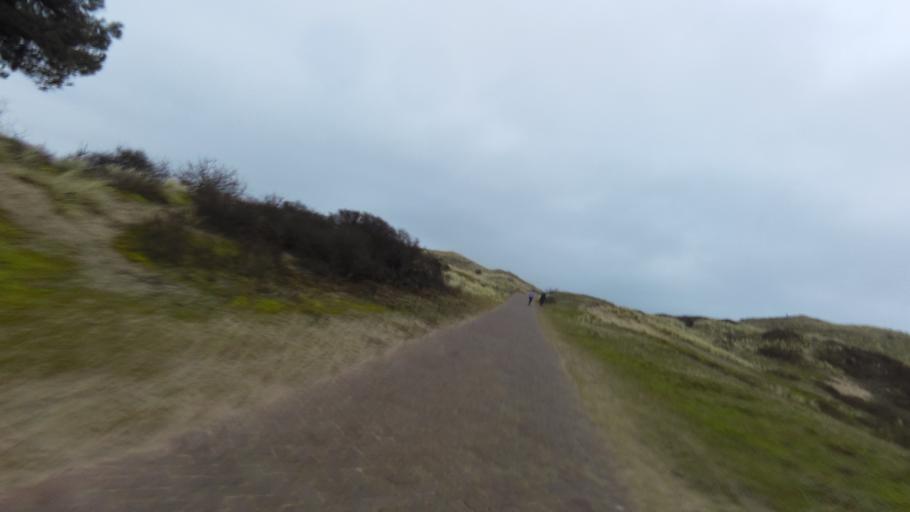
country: NL
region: North Holland
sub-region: Gemeente Bergen
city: Egmond aan Zee
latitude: 52.5969
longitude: 4.6222
